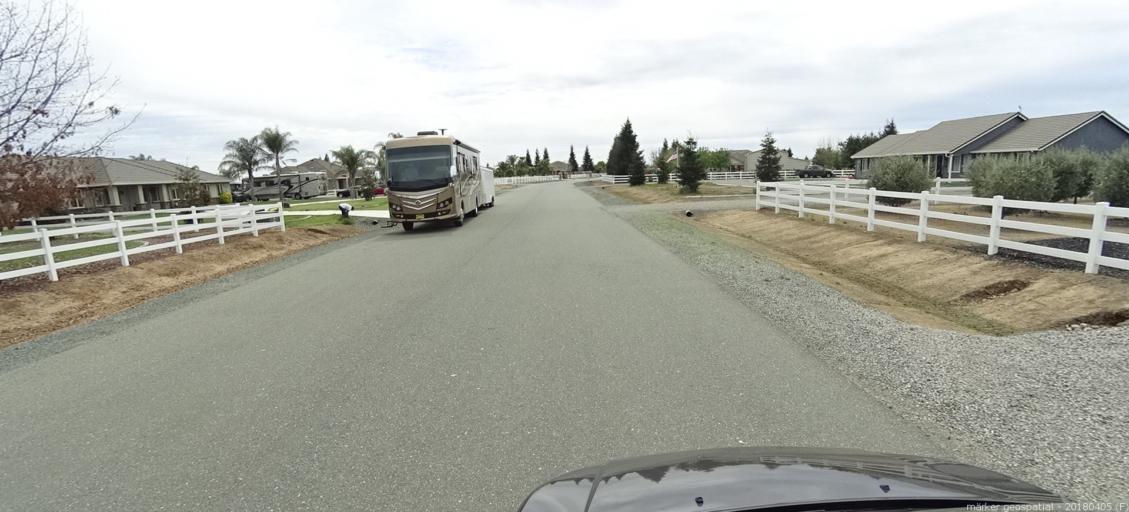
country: US
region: California
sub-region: Sacramento County
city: Galt
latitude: 38.2823
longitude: -121.3196
